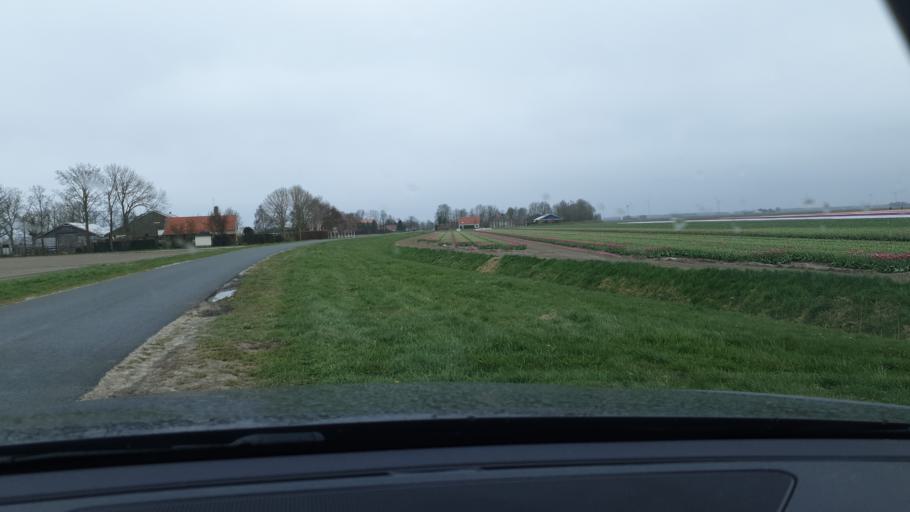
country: NL
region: Flevoland
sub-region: Gemeente Urk
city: Urk
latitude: 52.5653
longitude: 5.6018
